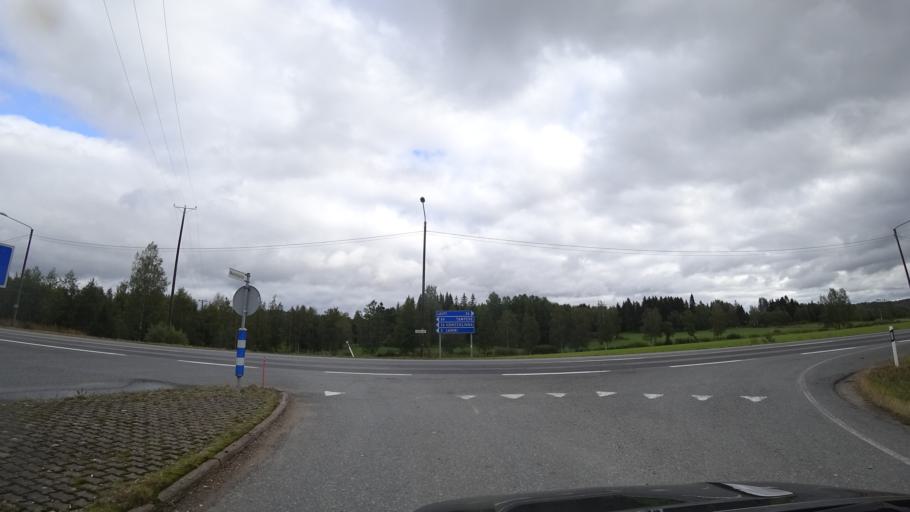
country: FI
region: Haeme
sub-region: Haemeenlinna
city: Lammi
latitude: 61.0515
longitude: 25.0088
